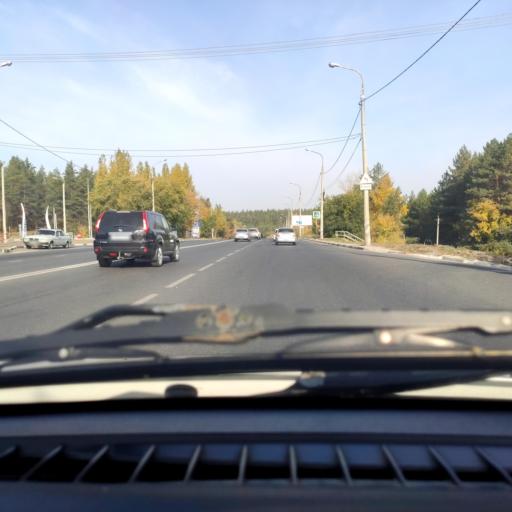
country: RU
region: Samara
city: Zhigulevsk
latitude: 53.4981
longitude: 49.4730
